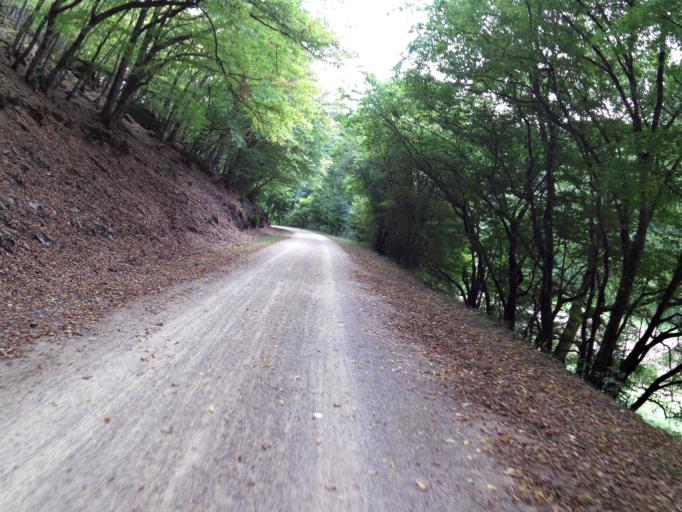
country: DE
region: North Rhine-Westphalia
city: Heimbach
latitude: 50.5833
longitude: 6.4623
